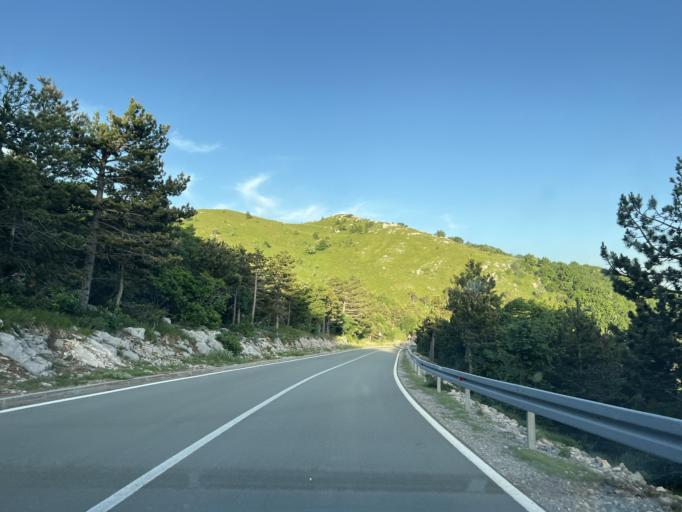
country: HR
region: Primorsko-Goranska
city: Cernik
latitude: 45.3964
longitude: 14.5527
